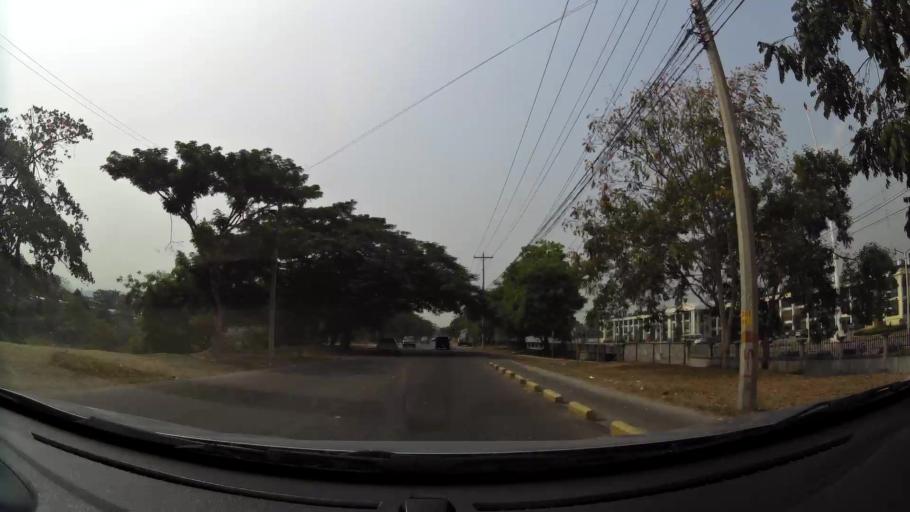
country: HN
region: Cortes
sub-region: San Pedro Sula
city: Pena Blanca
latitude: 15.5517
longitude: -88.0116
